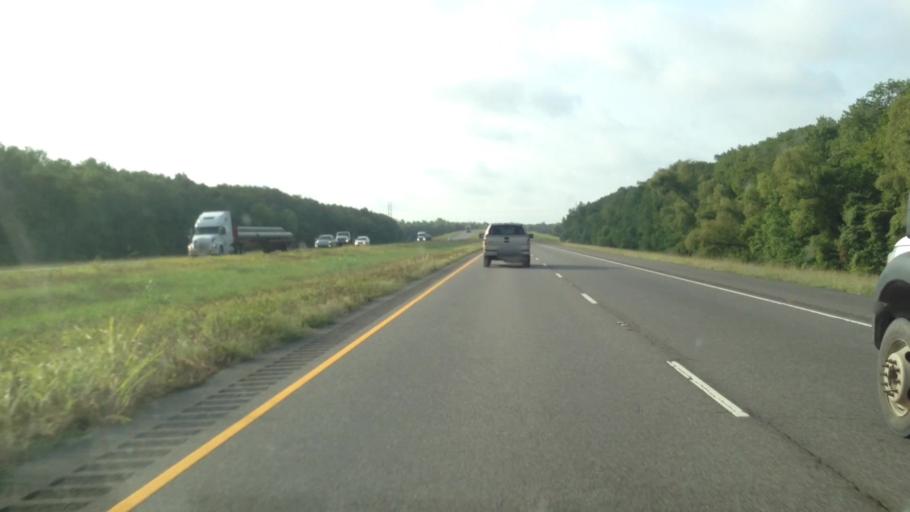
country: US
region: Louisiana
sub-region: Avoyelles Parish
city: Bunkie
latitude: 30.9049
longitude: -92.2342
